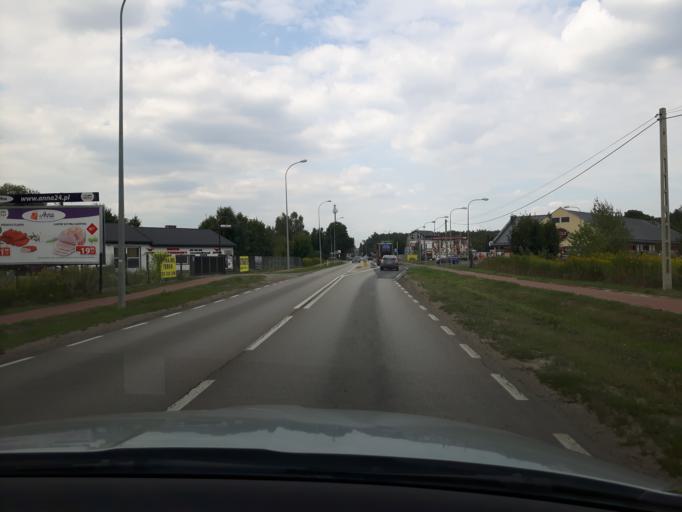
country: PL
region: Masovian Voivodeship
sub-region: Powiat legionowski
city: Stanislawow Pierwszy
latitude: 52.3759
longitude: 21.0291
